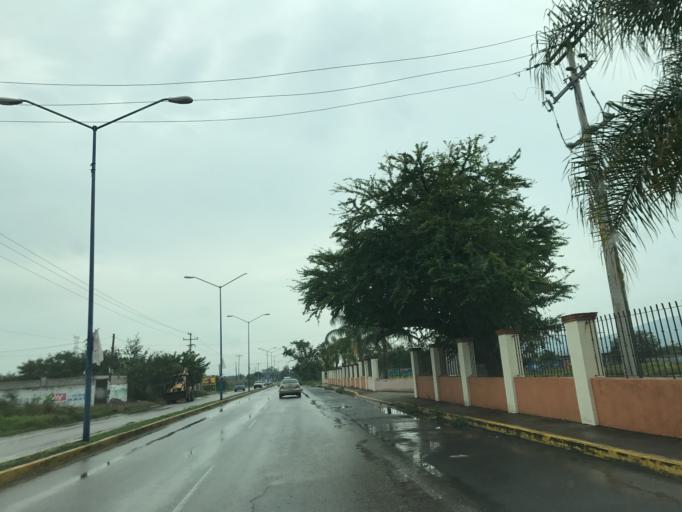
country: MX
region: Morelos
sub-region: Ayala
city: Olintepec
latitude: 18.7531
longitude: -98.9852
